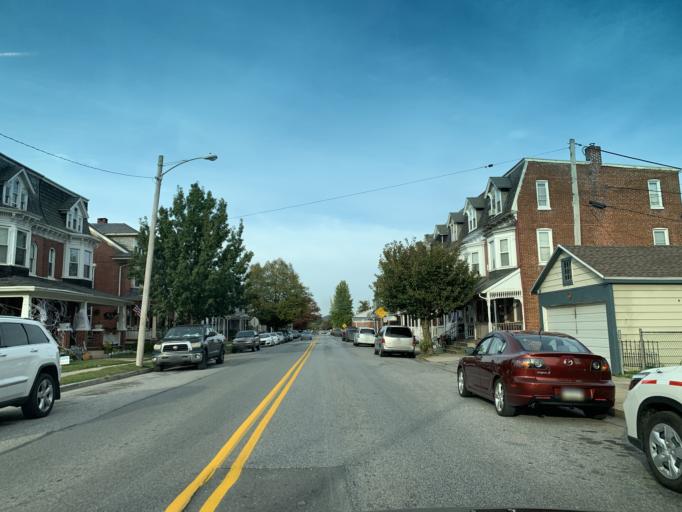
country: US
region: Pennsylvania
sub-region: York County
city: West York
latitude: 39.9629
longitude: -76.7488
